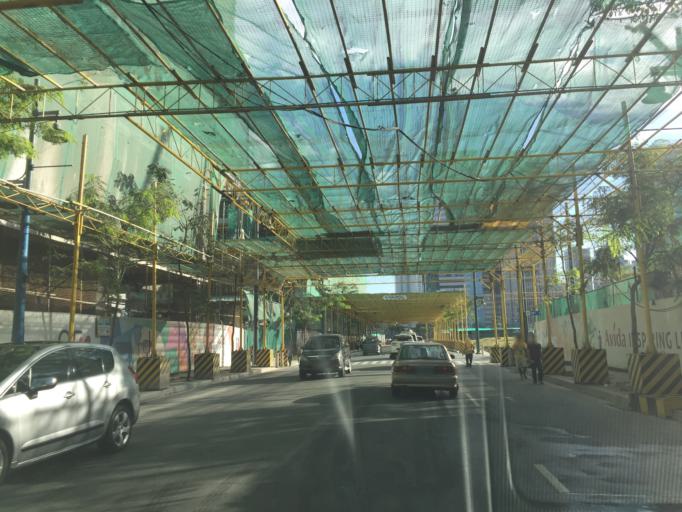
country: PH
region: Metro Manila
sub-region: Makati City
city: Makati City
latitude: 14.5562
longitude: 121.0531
